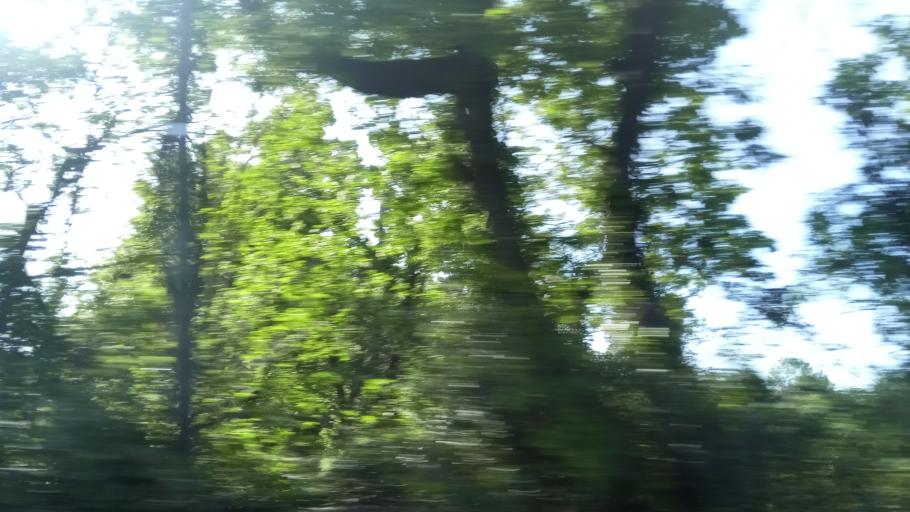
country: IT
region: Latium
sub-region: Provincia di Latina
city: Grunuovo-Campomaggiore San Luca
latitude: 41.2605
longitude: 13.7759
